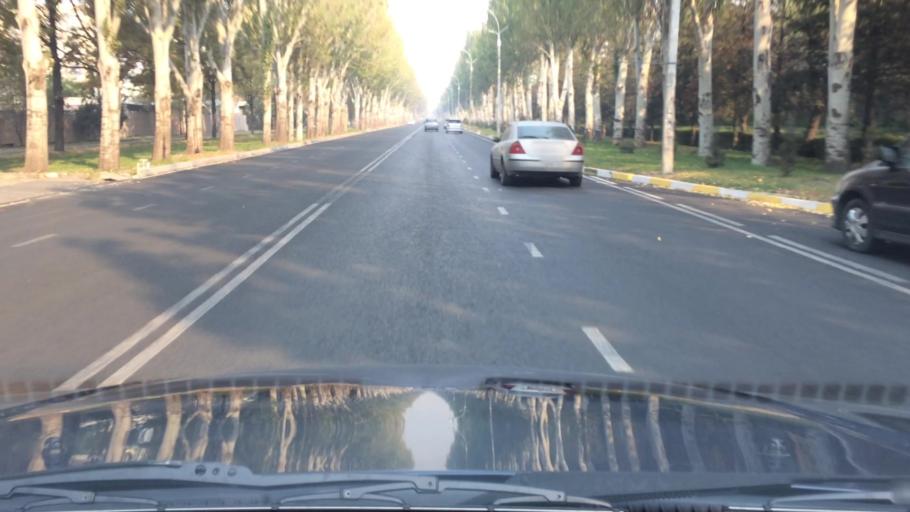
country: KG
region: Chuy
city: Bishkek
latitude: 42.8331
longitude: 74.5855
